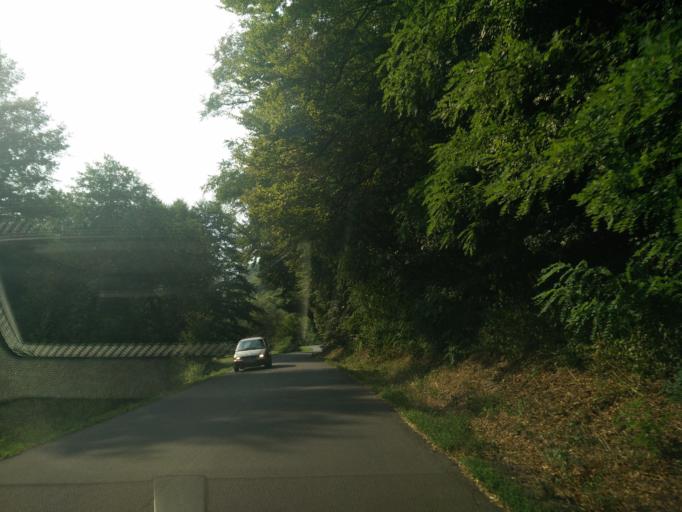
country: SK
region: Banskobystricky
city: Zarnovica
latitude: 48.5200
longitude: 18.7684
